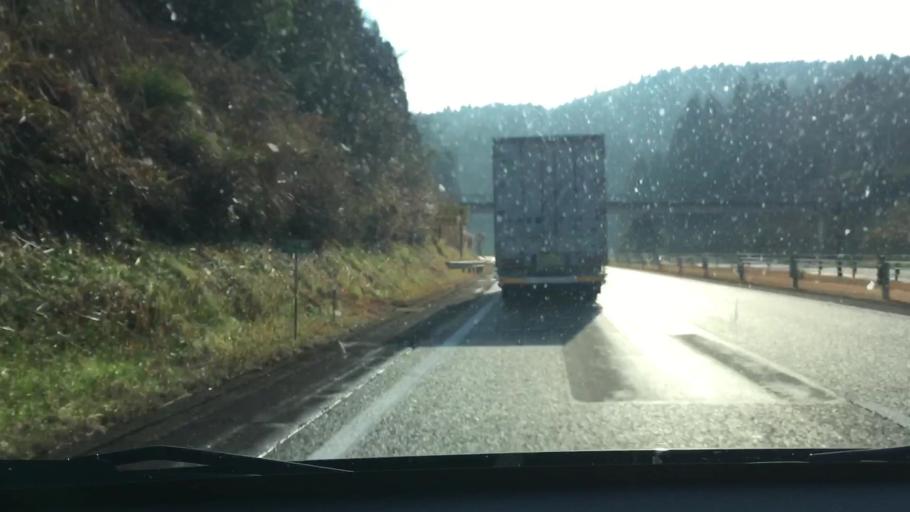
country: JP
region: Kagoshima
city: Okuchi-shinohara
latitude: 31.9849
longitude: 130.7528
